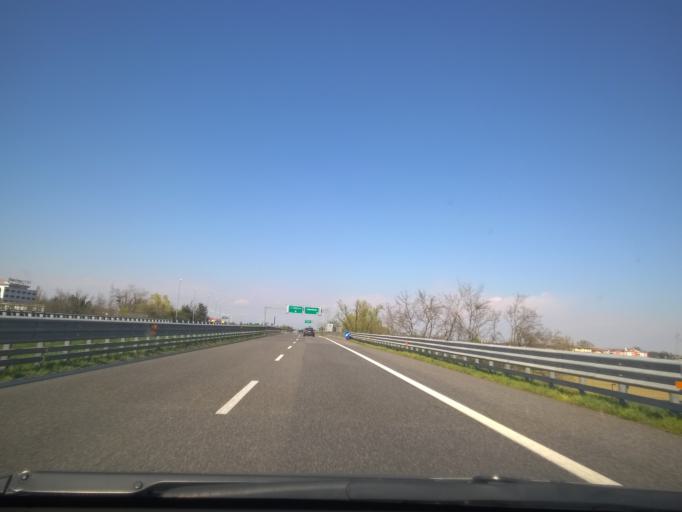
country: IT
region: Lombardy
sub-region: Provincia di Cremona
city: San Felice
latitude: 45.1371
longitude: 10.0703
